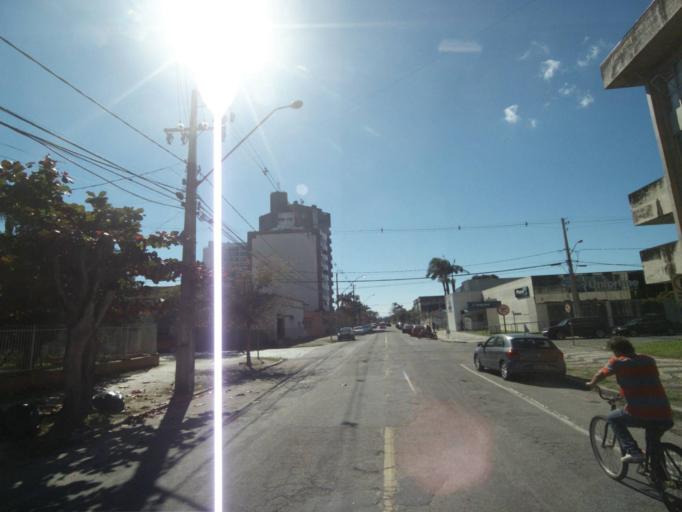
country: BR
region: Parana
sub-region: Paranagua
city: Paranagua
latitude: -25.5159
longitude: -48.5044
